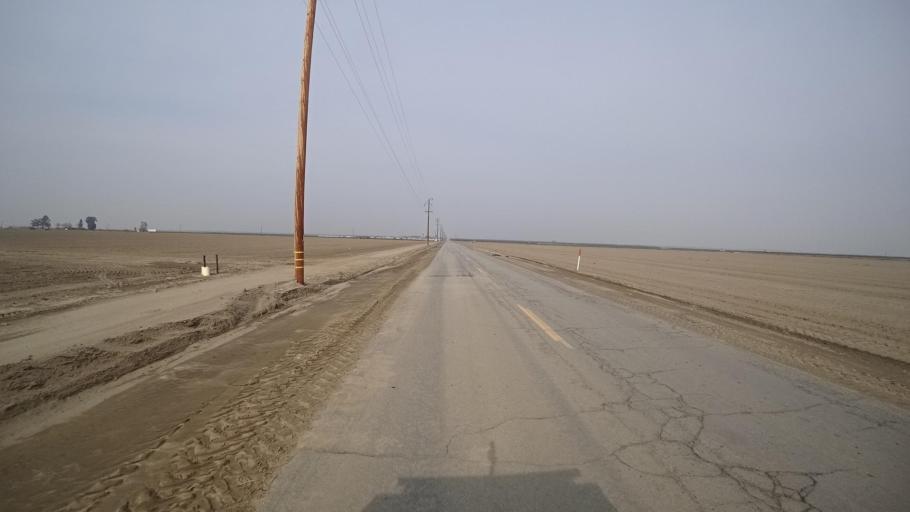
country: US
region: California
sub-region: Kern County
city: Arvin
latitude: 35.1541
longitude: -118.8781
